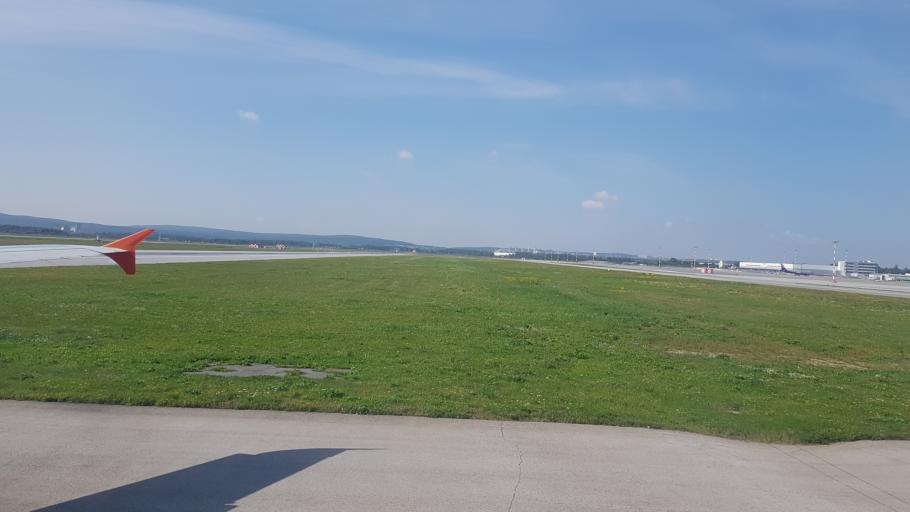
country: RU
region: Sverdlovsk
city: Istok
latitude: 56.7457
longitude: 60.8065
